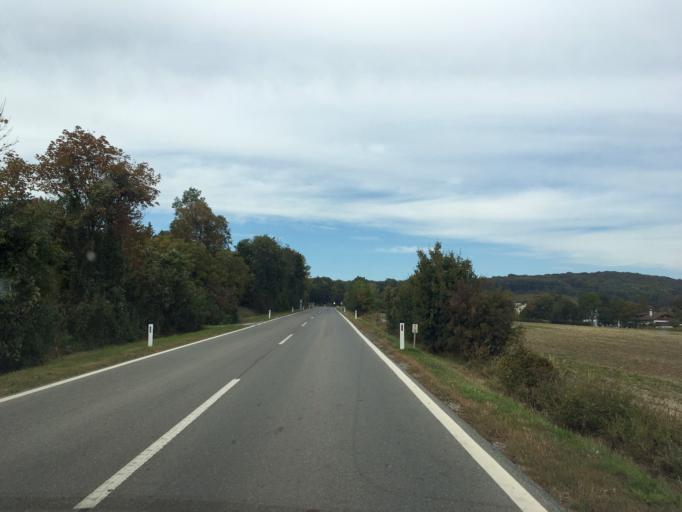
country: AT
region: Burgenland
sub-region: Eisenstadt-Umgebung
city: Breitenbrunn
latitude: 47.9572
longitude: 16.7376
